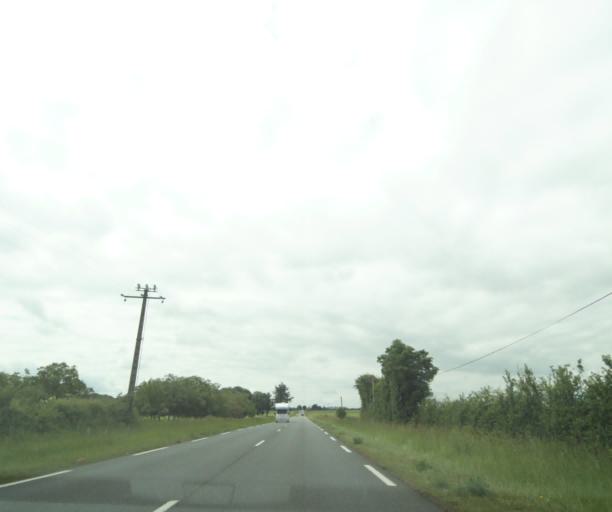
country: FR
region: Pays de la Loire
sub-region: Departement de Maine-et-Loire
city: Montreuil-Bellay
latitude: 47.1523
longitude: -0.1482
